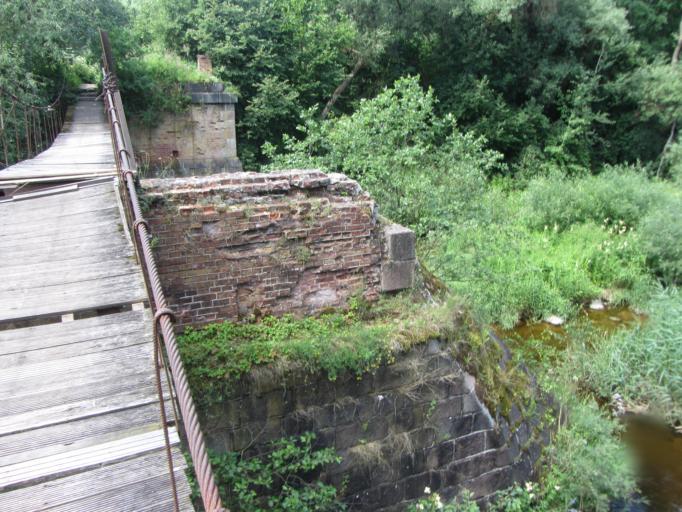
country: LT
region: Kauno apskritis
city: Kedainiai
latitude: 55.2612
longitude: 23.8118
